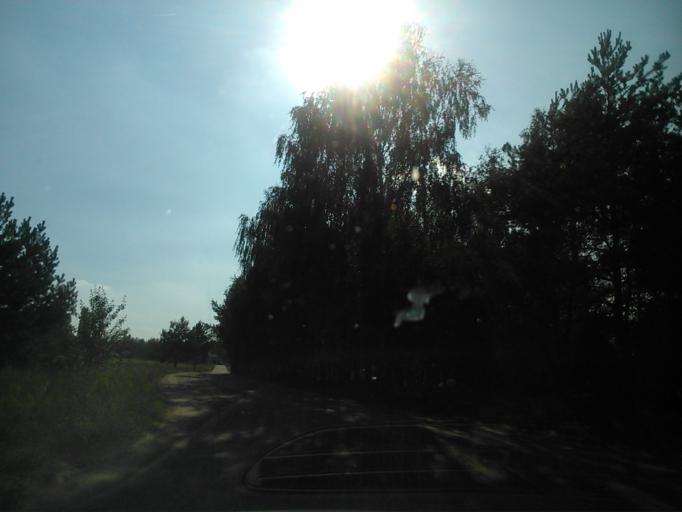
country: PL
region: Kujawsko-Pomorskie
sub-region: Powiat golubsko-dobrzynski
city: Golub-Dobrzyn
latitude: 53.1134
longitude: 19.0748
